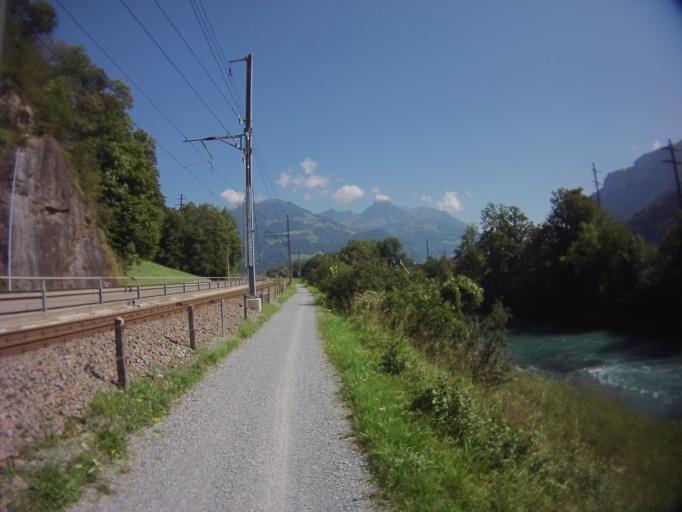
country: CH
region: Glarus
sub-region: Glarus
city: Niederurnen
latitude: 47.1409
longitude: 9.0521
